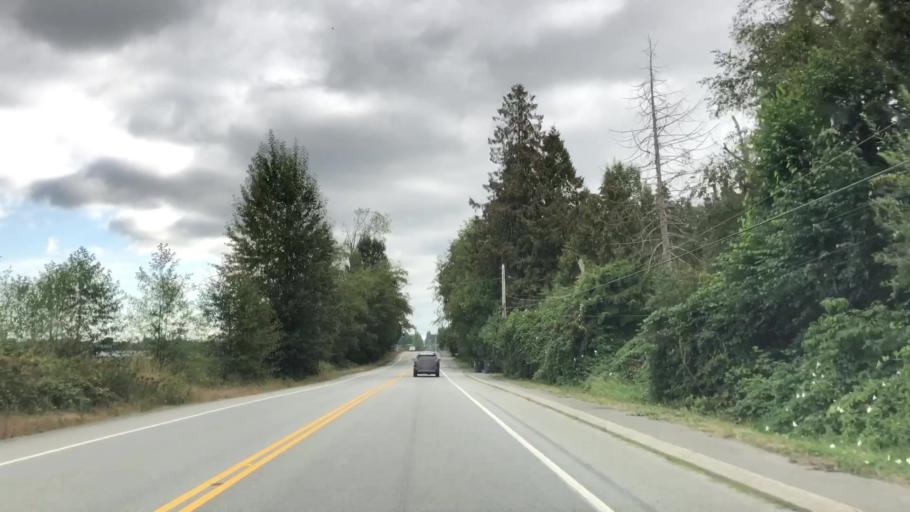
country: US
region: Washington
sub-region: Whatcom County
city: Blaine
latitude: 49.0601
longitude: -122.7414
